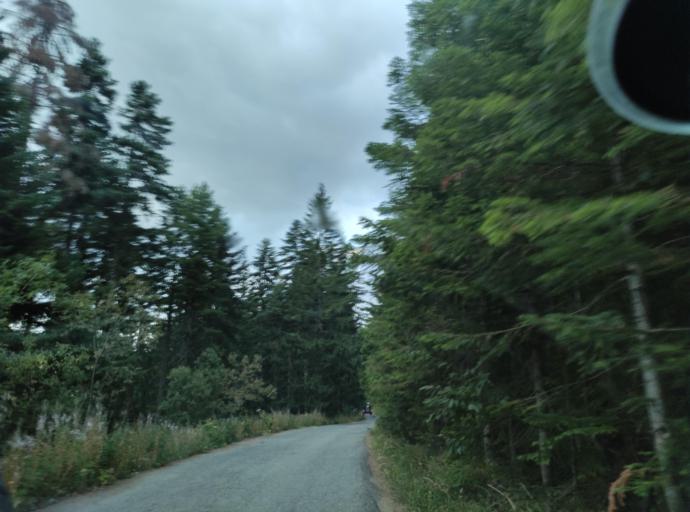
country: BG
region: Blagoevgrad
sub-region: Obshtina Bansko
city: Bansko
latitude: 41.7772
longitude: 23.4394
